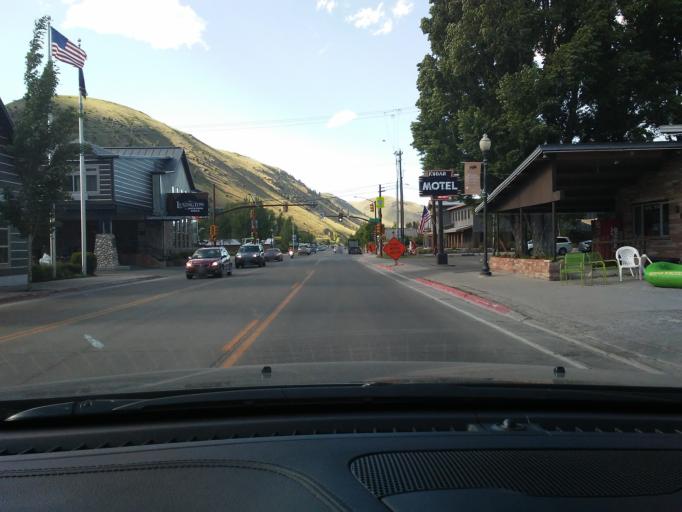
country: US
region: Wyoming
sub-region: Teton County
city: Jackson
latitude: 43.4827
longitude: -110.7624
